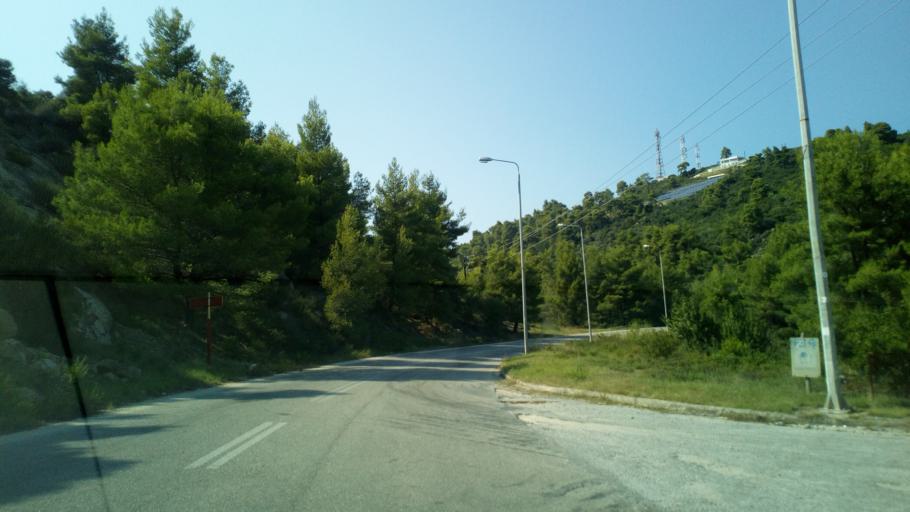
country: GR
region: Central Macedonia
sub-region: Nomos Chalkidikis
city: Sarti
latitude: 40.1031
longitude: 23.9793
